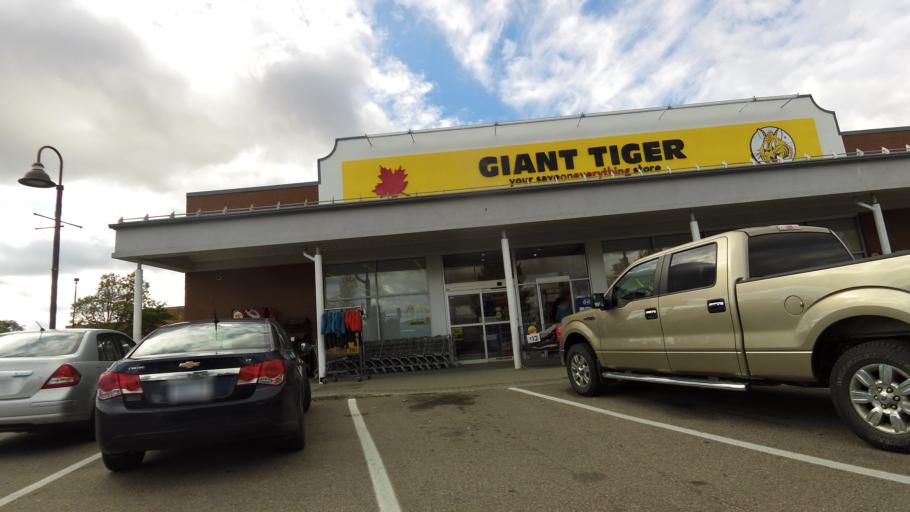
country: CA
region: Ontario
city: Deep River
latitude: 46.1020
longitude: -77.4875
